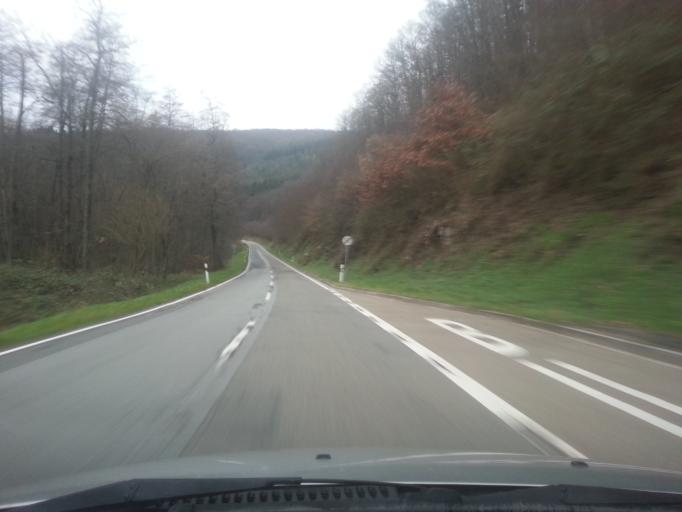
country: DE
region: Baden-Wuerttemberg
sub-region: Karlsruhe Region
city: Eberbach
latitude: 49.4865
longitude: 9.0341
